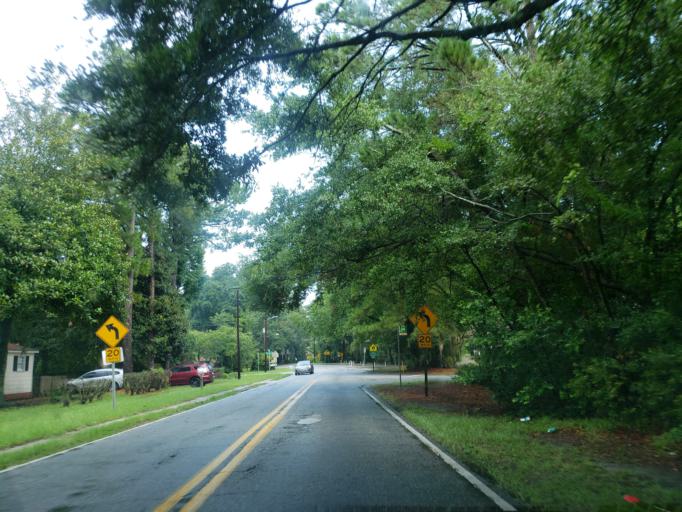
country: US
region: Georgia
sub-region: Chatham County
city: Thunderbolt
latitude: 32.0309
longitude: -81.0723
